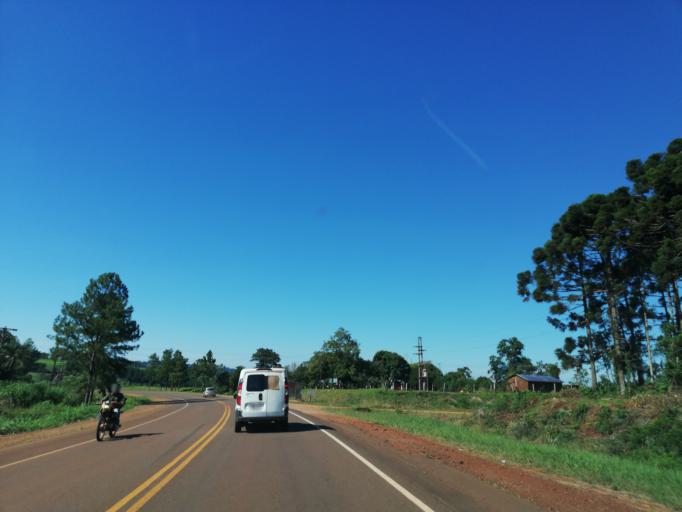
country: AR
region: Misiones
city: Dos de Mayo
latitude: -27.0616
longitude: -54.4267
